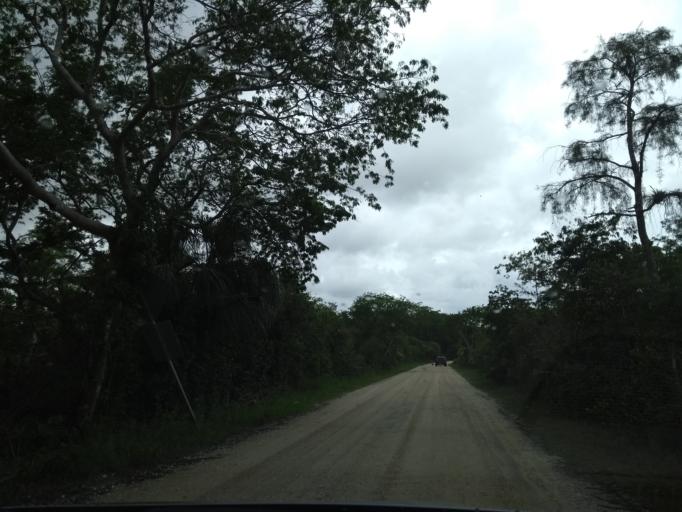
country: US
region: Florida
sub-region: Miami-Dade County
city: The Hammocks
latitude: 25.7466
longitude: -80.9524
